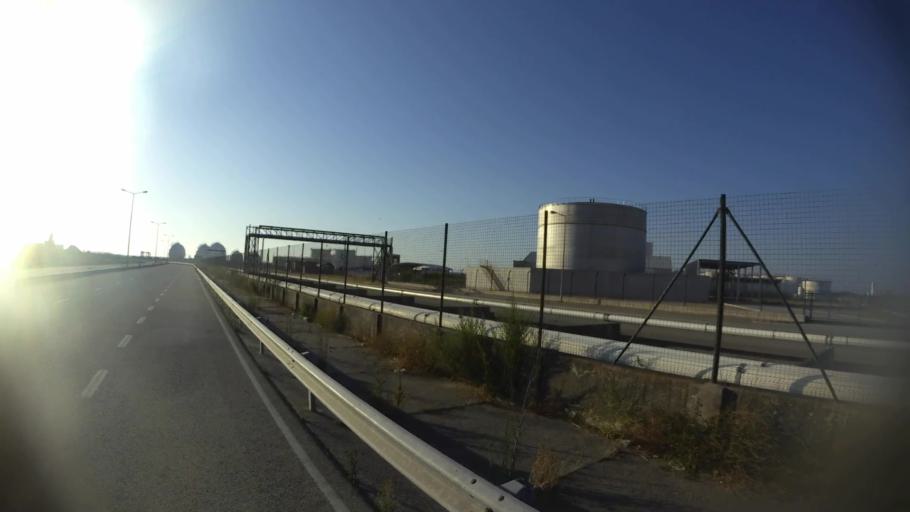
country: PT
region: Aveiro
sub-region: Ilhavo
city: Gafanha da Nazare
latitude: 40.6536
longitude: -8.7091
